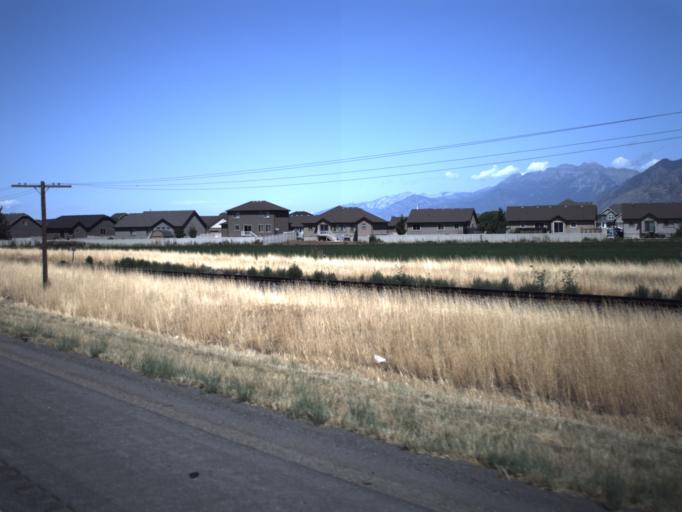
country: US
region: Utah
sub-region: Utah County
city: Spanish Fork
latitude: 40.1011
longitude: -111.6156
